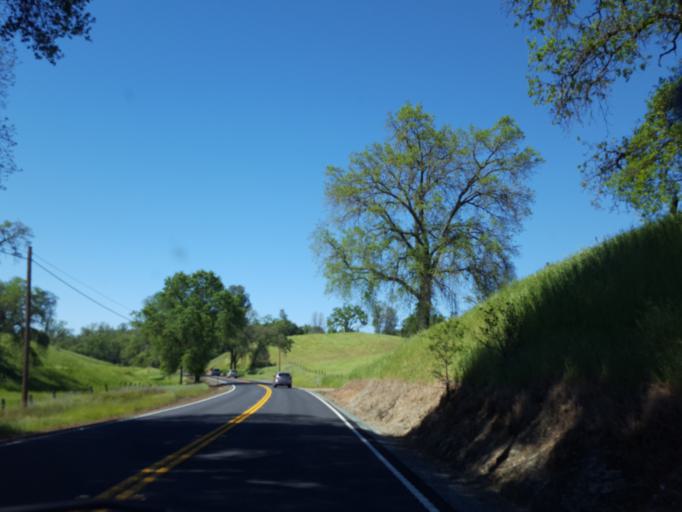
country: US
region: California
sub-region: Calaveras County
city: San Andreas
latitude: 38.1521
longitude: -120.6421
